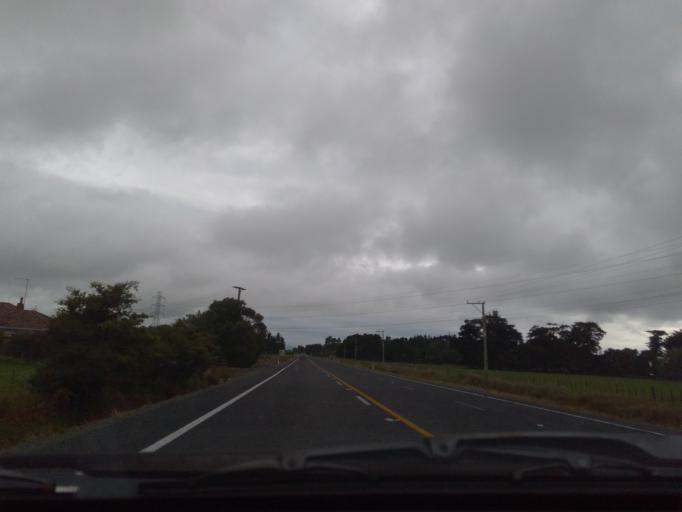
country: NZ
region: Northland
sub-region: Whangarei
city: Ruakaka
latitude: -35.9912
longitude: 174.4238
